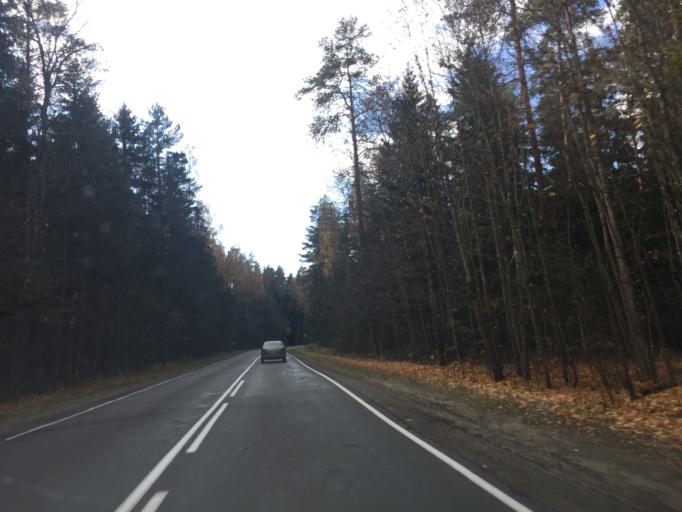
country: BY
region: Minsk
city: Svir
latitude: 54.9233
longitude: 26.5277
